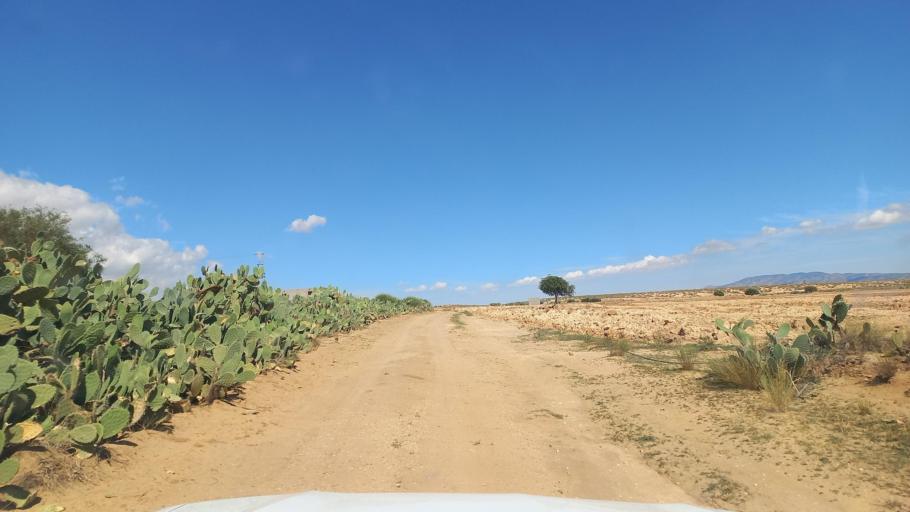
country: TN
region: Al Qasrayn
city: Sbiba
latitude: 35.3467
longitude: 9.0140
